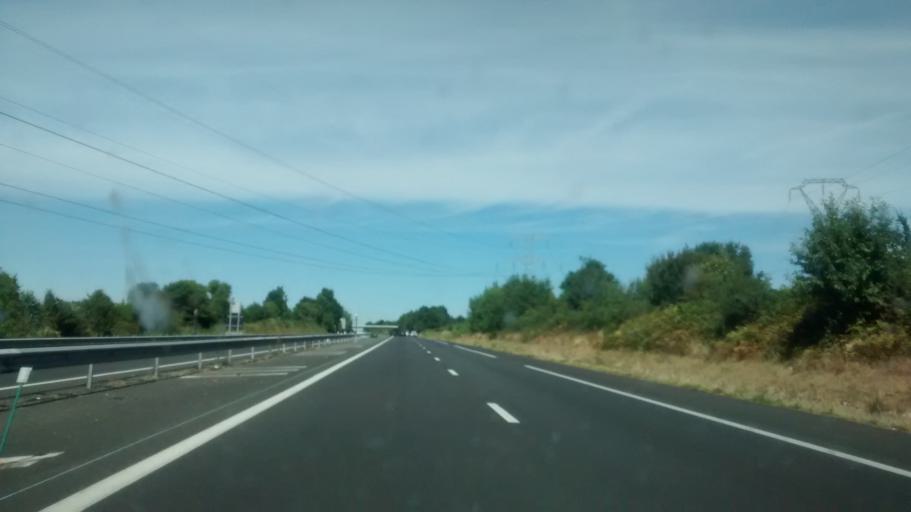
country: FR
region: Poitou-Charentes
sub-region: Departement de la Charente-Maritime
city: Thenac
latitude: 45.6210
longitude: -0.6081
